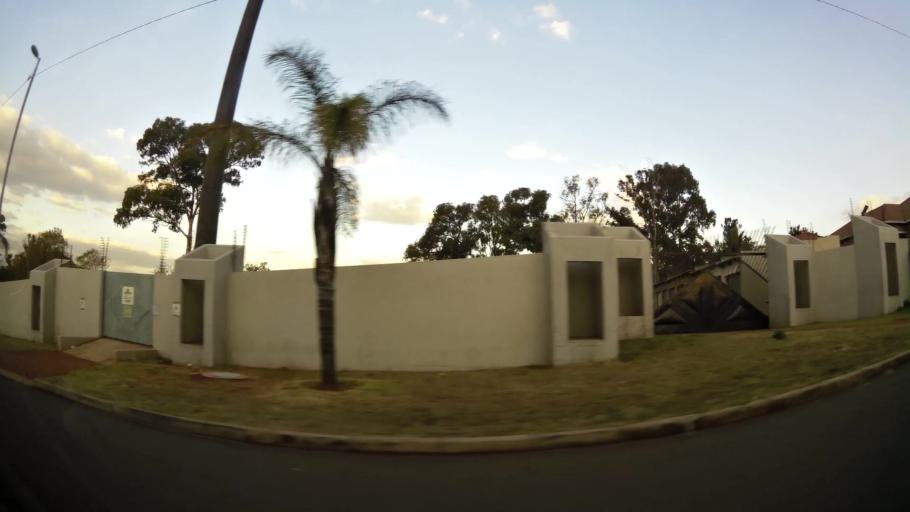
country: ZA
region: Gauteng
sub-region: West Rand District Municipality
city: Krugersdorp
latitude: -26.0681
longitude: 27.7936
